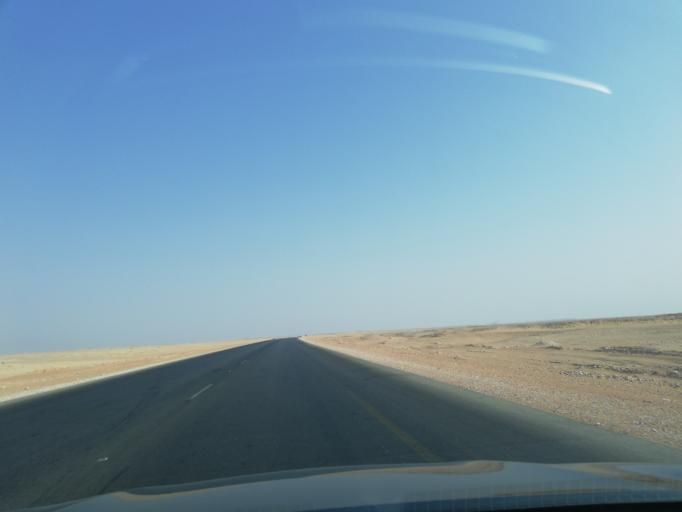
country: OM
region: Zufar
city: Salalah
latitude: 17.7740
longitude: 54.0144
